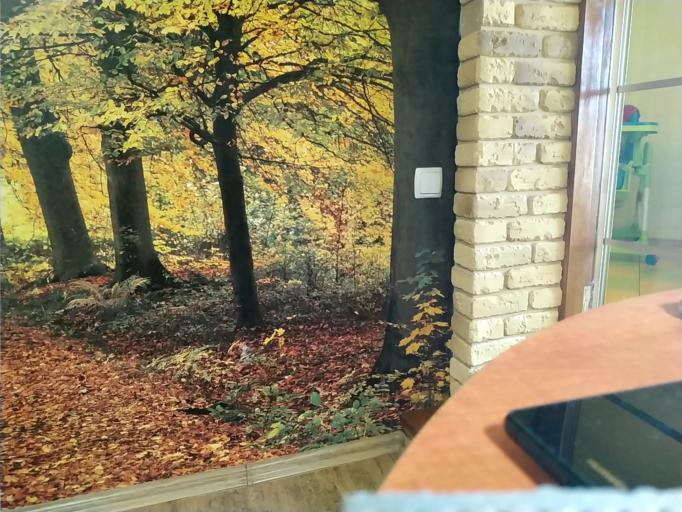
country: RU
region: Kaluga
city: Kondrovo
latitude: 54.8054
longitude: 35.9521
